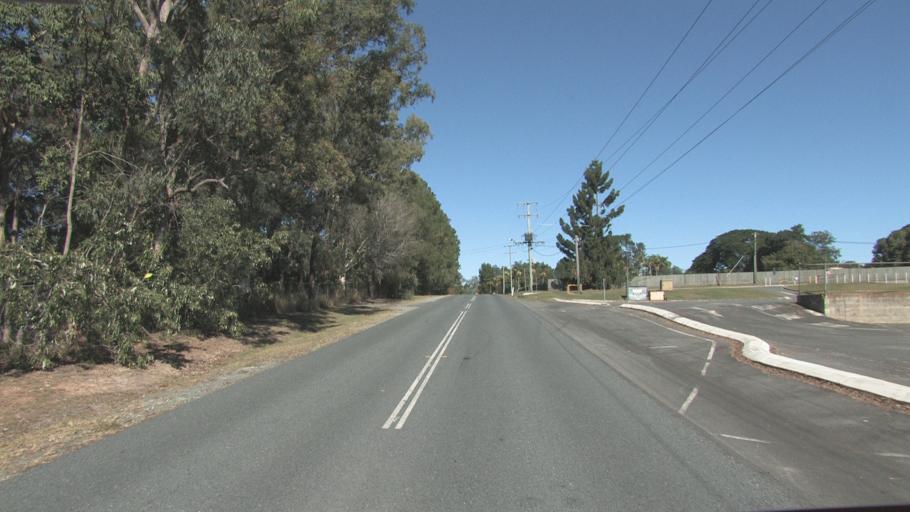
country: AU
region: Queensland
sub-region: Logan
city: Park Ridge South
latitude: -27.7055
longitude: 153.0586
